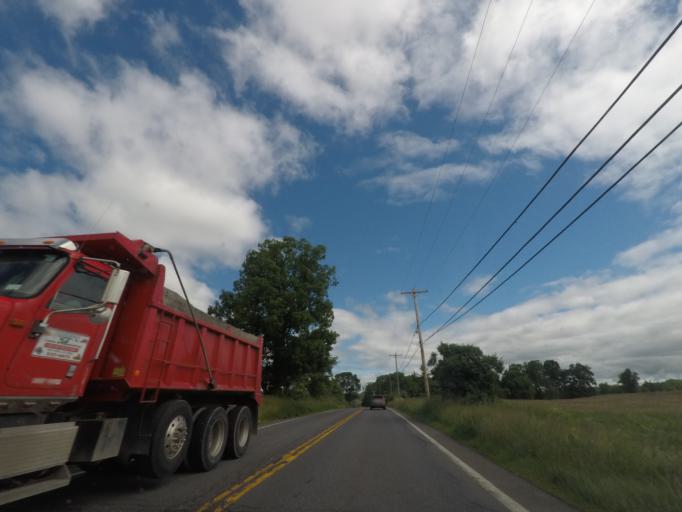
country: US
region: New York
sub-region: Columbia County
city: Philmont
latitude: 42.2153
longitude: -73.7061
